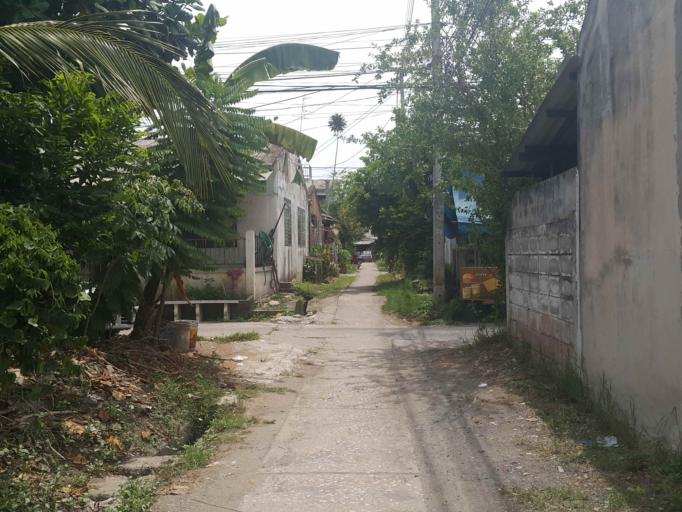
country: TH
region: Chiang Mai
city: Chiang Mai
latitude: 18.7607
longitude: 99.0124
